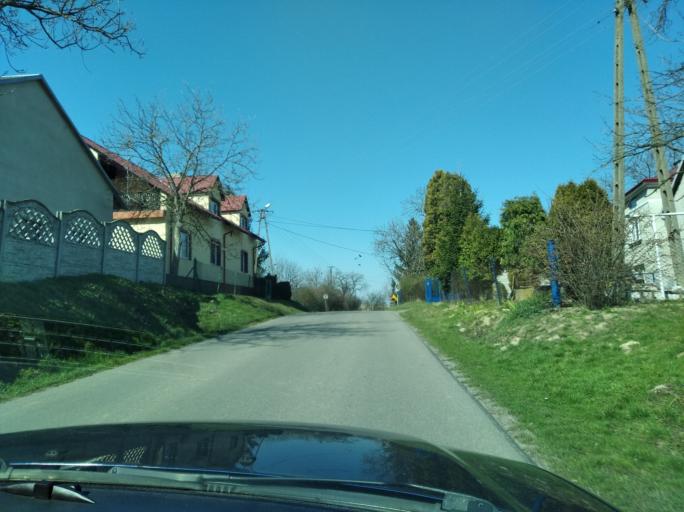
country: PL
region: Subcarpathian Voivodeship
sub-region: Powiat przeworski
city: Pantalowice
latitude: 49.9504
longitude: 22.4368
